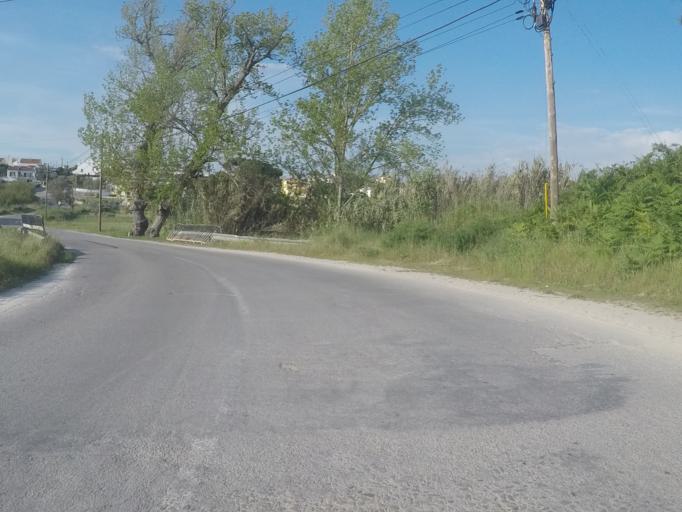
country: PT
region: Setubal
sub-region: Sesimbra
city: Sesimbra
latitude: 38.4745
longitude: -9.1656
